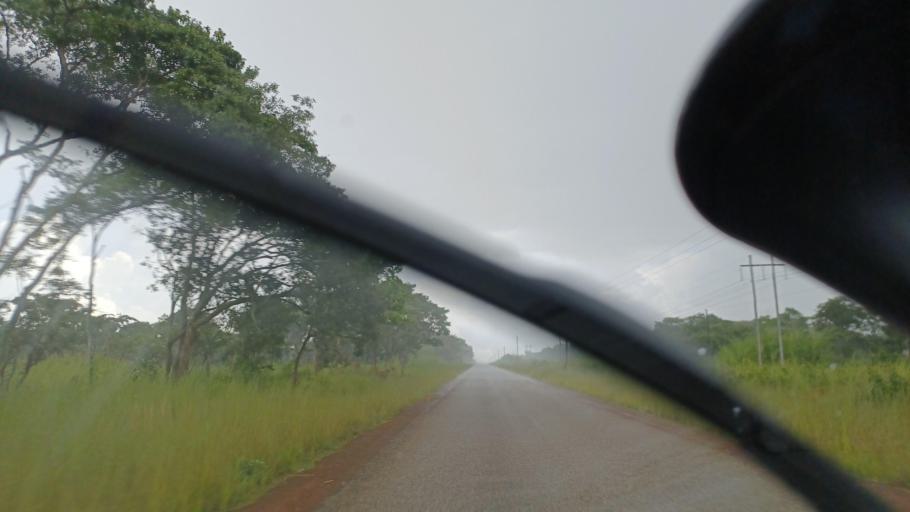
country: ZM
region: North-Western
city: Kasempa
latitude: -13.0931
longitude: 25.9213
